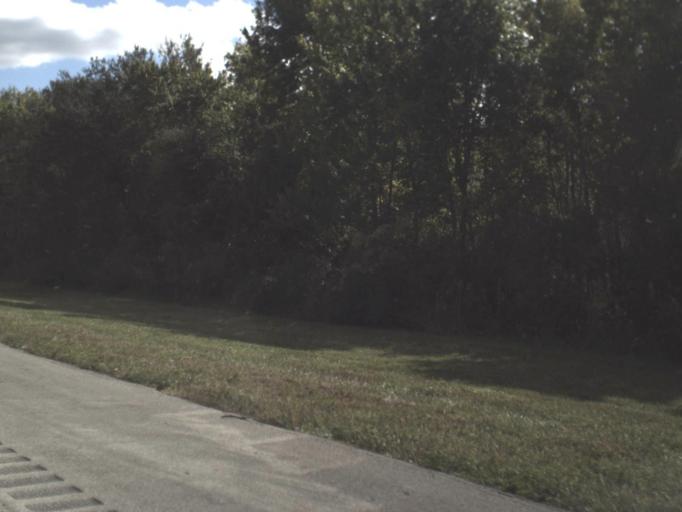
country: US
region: Florida
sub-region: Indian River County
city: Fellsmere
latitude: 27.6113
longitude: -80.8301
